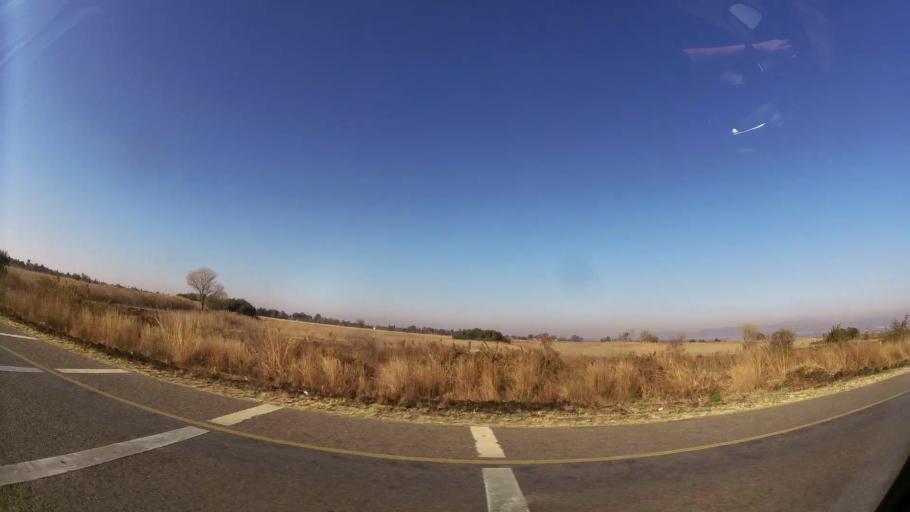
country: ZA
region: Gauteng
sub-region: City of Johannesburg Metropolitan Municipality
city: Johannesburg
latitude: -26.3125
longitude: 28.0827
